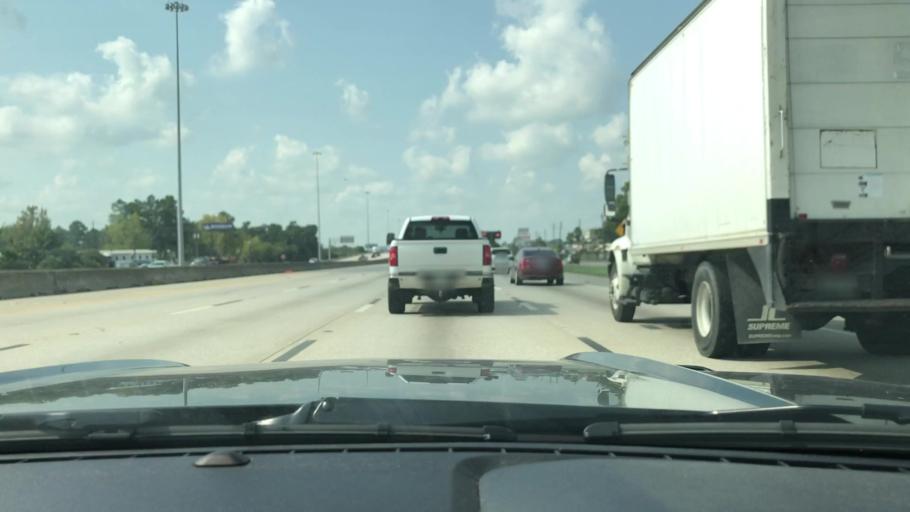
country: US
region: Texas
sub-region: Harris County
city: Aldine
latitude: 29.8967
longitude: -95.3149
